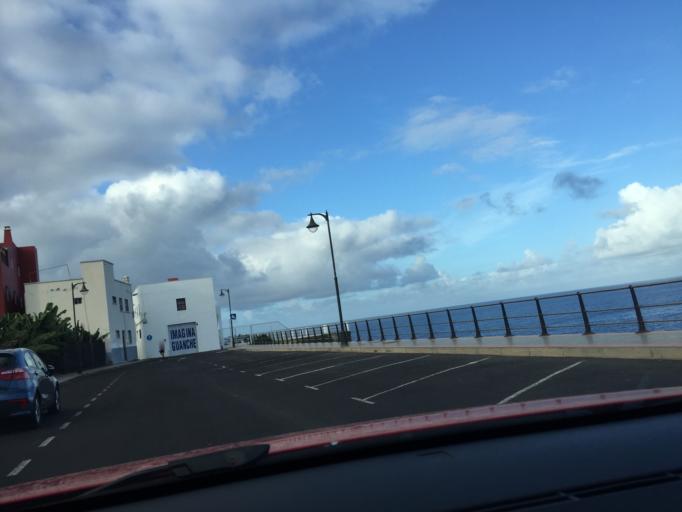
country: ES
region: Canary Islands
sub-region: Provincia de Santa Cruz de Tenerife
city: Garachico
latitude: 28.8070
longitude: -17.7621
